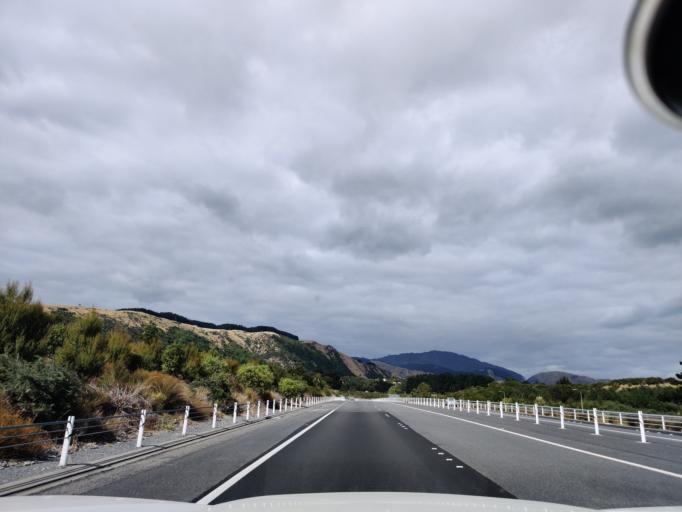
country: NZ
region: Wellington
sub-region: Kapiti Coast District
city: Paraparaumu
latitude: -40.9250
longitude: 174.9921
